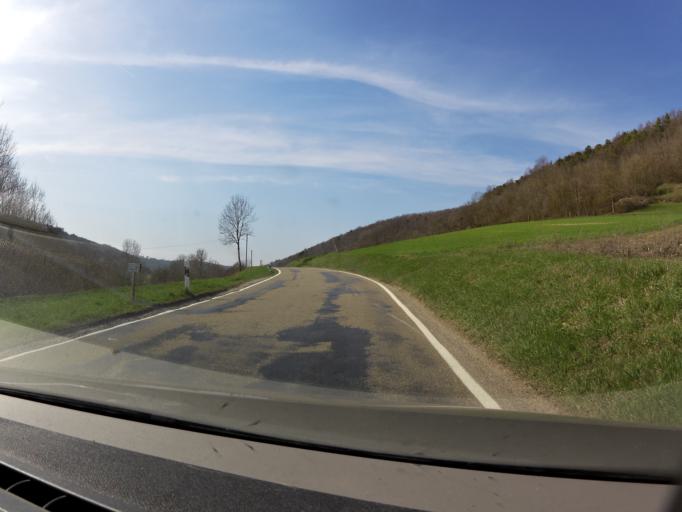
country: DE
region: Bavaria
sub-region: Regierungsbezirk Mittelfranken
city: Adelshofen
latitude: 49.4466
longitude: 10.1016
